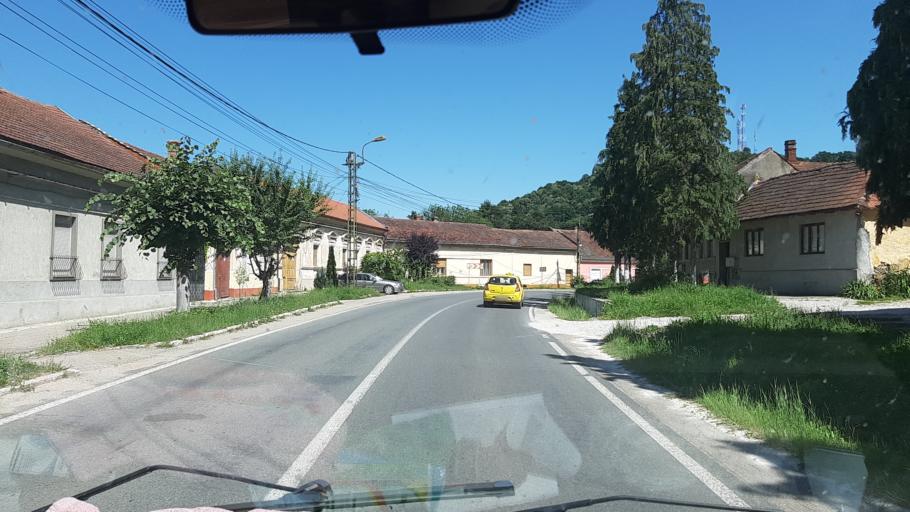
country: RO
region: Caras-Severin
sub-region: Oras Bocsa
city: Bocsa
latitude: 45.3797
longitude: 21.7705
